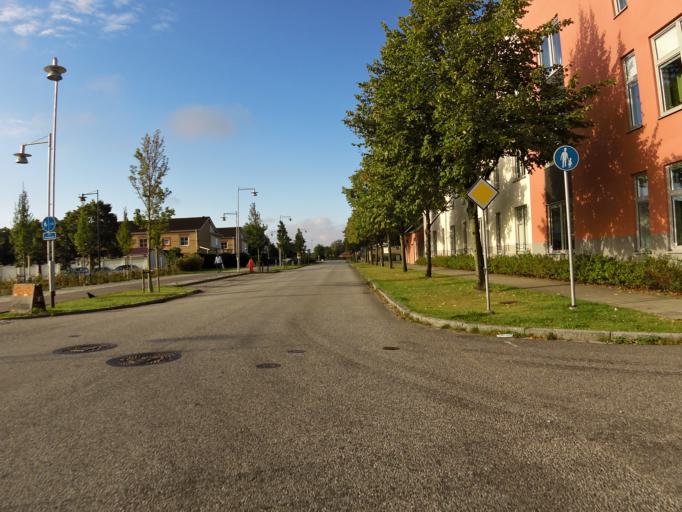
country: SE
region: Skane
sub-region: Lomma Kommun
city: Lomma
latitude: 55.6723
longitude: 13.0676
